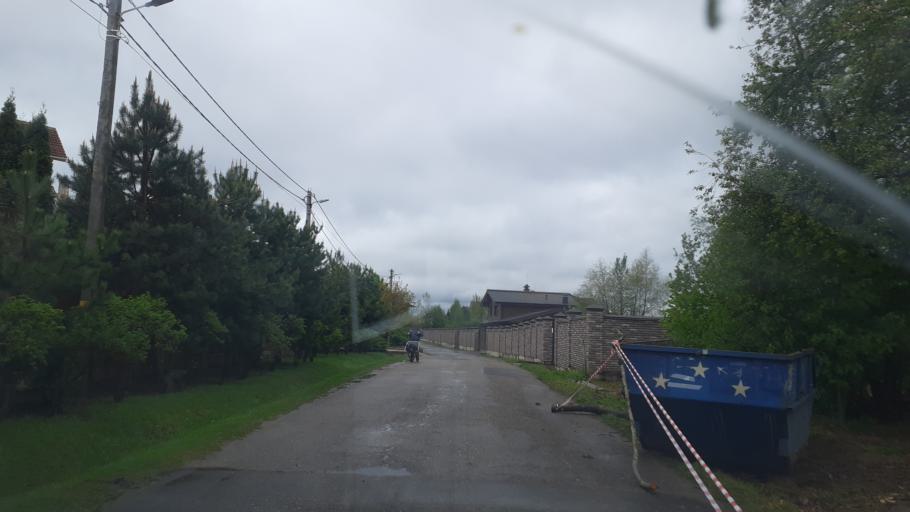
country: RU
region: Moskovskaya
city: Gorki Vtoryye
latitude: 55.7047
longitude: 37.2009
